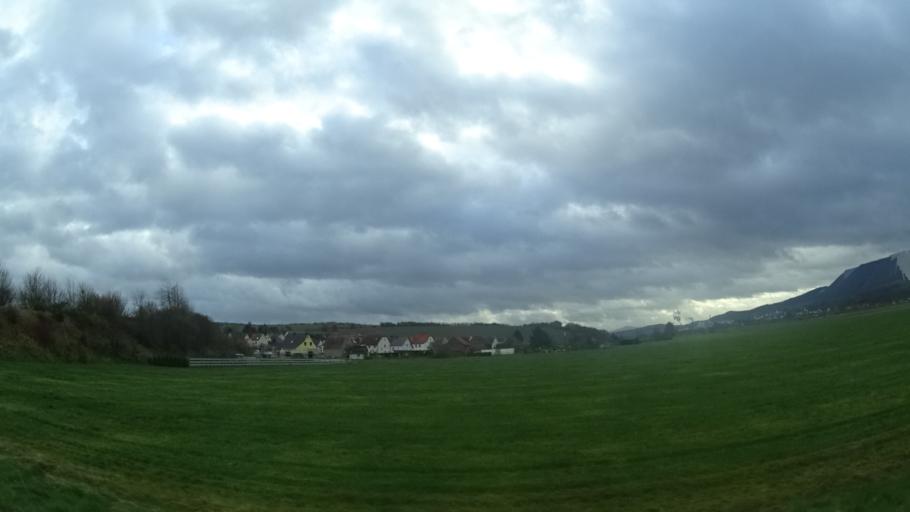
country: DE
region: Thuringia
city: Dippach
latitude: 50.9206
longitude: 10.0392
